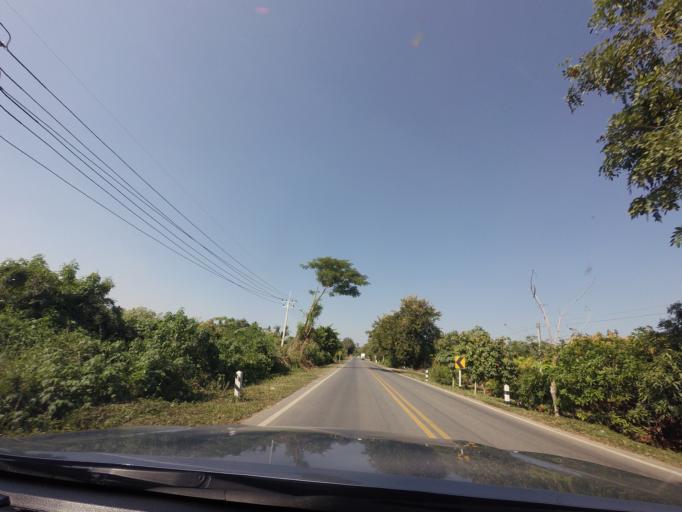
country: TH
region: Sukhothai
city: Sawankhalok
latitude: 17.3408
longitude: 99.8267
